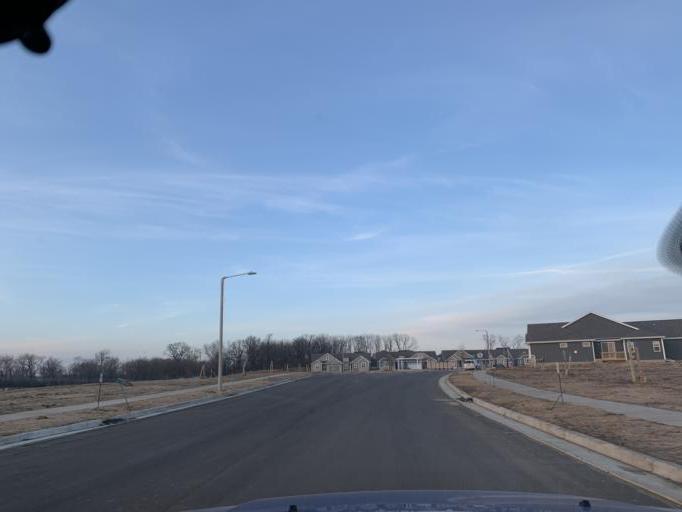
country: US
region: Wisconsin
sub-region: Dane County
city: Verona
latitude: 43.0506
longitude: -89.5649
